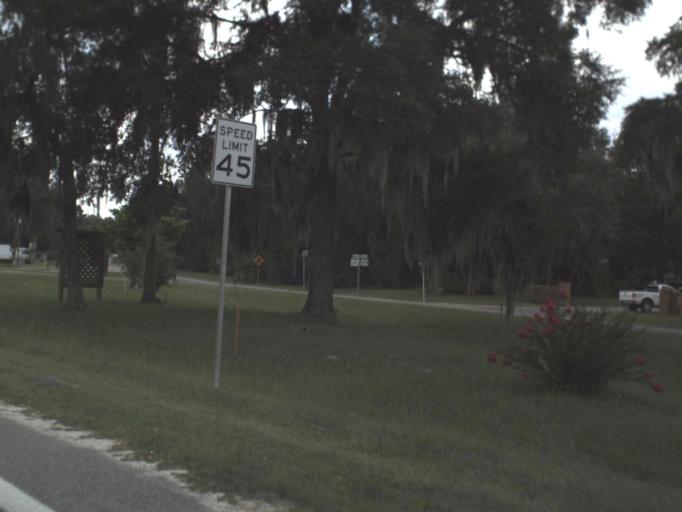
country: US
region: Florida
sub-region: Hamilton County
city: Jasper
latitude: 30.5244
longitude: -82.9616
